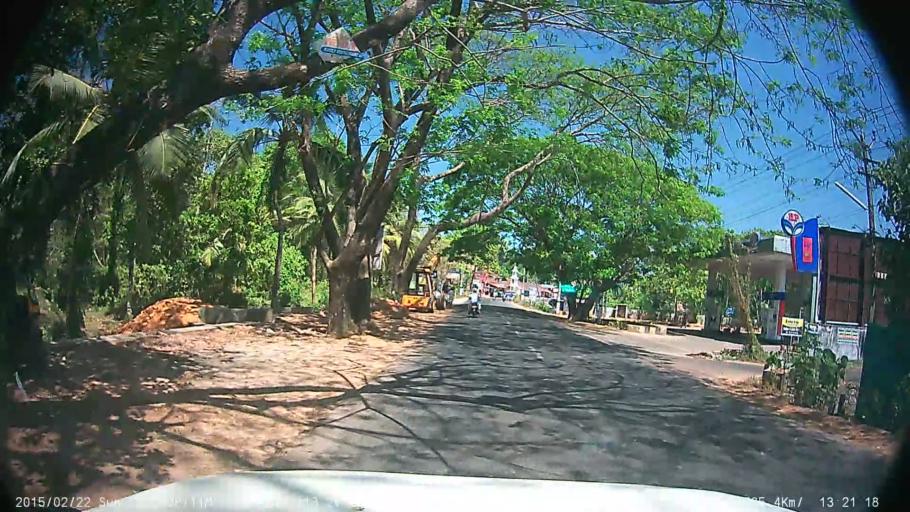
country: IN
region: Kerala
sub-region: Kottayam
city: Changanacheri
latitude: 9.4770
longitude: 76.5810
